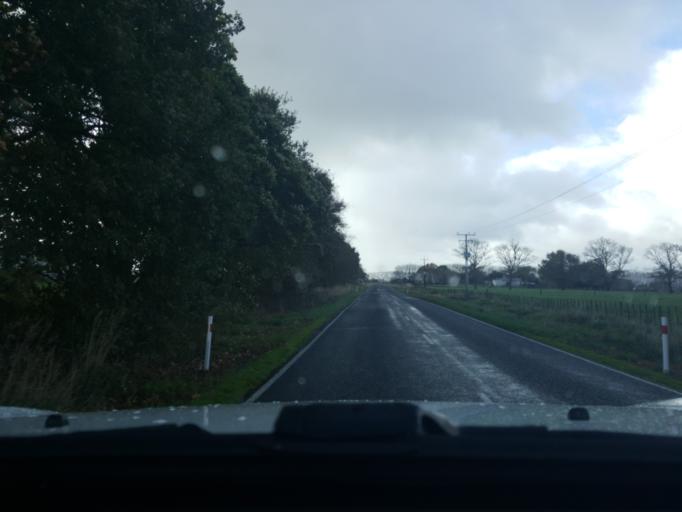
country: NZ
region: Waikato
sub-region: Waikato District
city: Te Kauwhata
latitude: -37.4459
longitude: 175.1139
